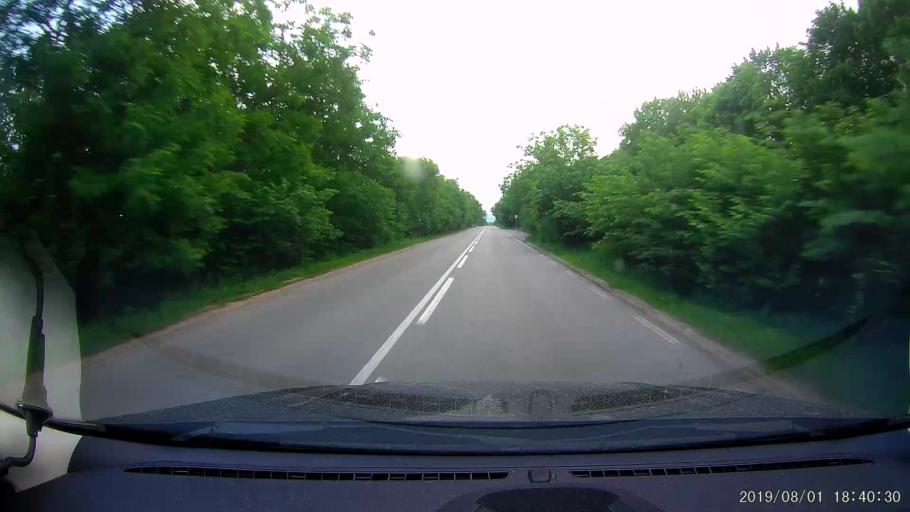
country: BG
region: Shumen
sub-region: Obshtina Khitrino
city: Gara Khitrino
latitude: 43.3658
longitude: 26.9194
